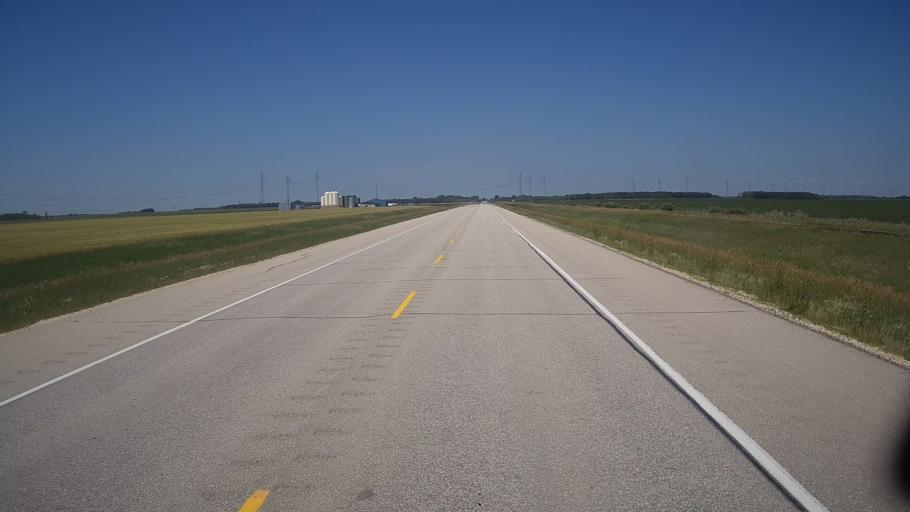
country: CA
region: Manitoba
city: Stonewall
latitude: 50.0466
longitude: -97.4151
